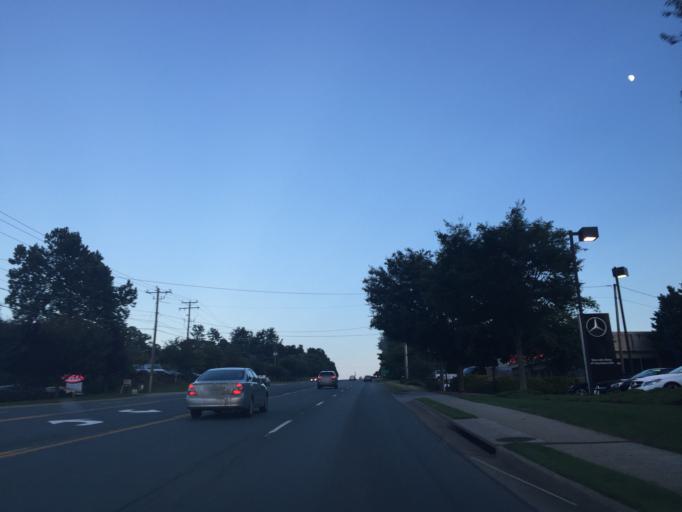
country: US
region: Virginia
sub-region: City of Charlottesville
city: Charlottesville
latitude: 38.0332
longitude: -78.4490
